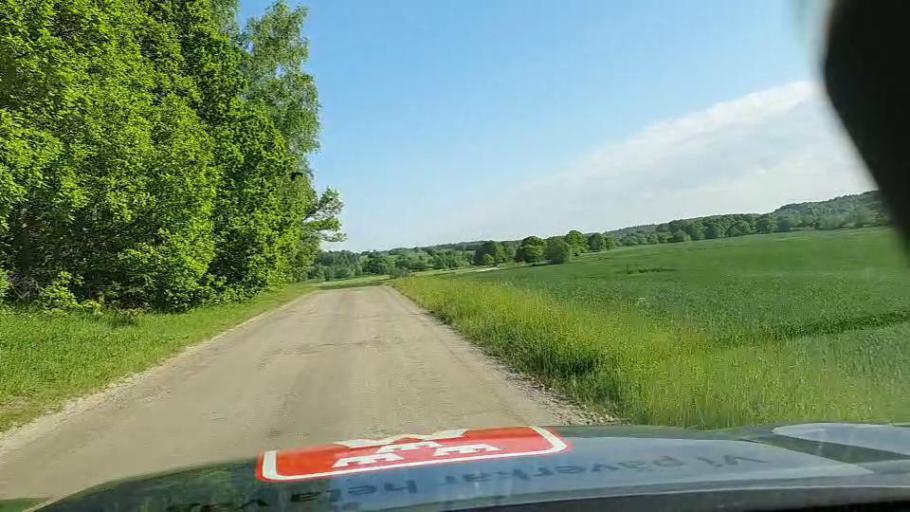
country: SE
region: Skane
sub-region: Hassleholms Kommun
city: Tormestorp
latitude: 56.1163
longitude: 13.7178
